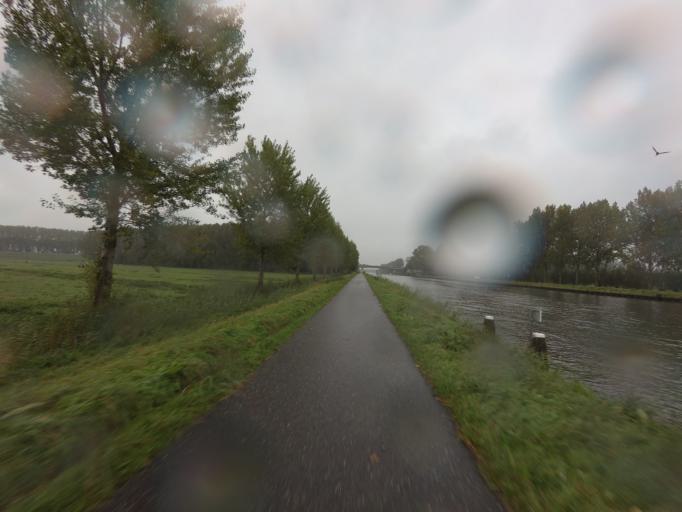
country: NL
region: Utrecht
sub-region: Gemeente Vianen
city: Vianen
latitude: 51.9524
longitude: 5.0525
